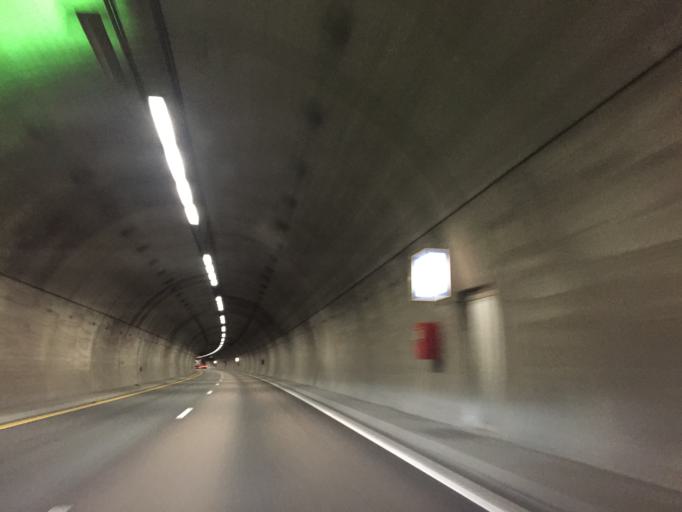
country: NO
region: Akershus
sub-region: Oppegard
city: Kolbotn
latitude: 59.7718
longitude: 10.8316
